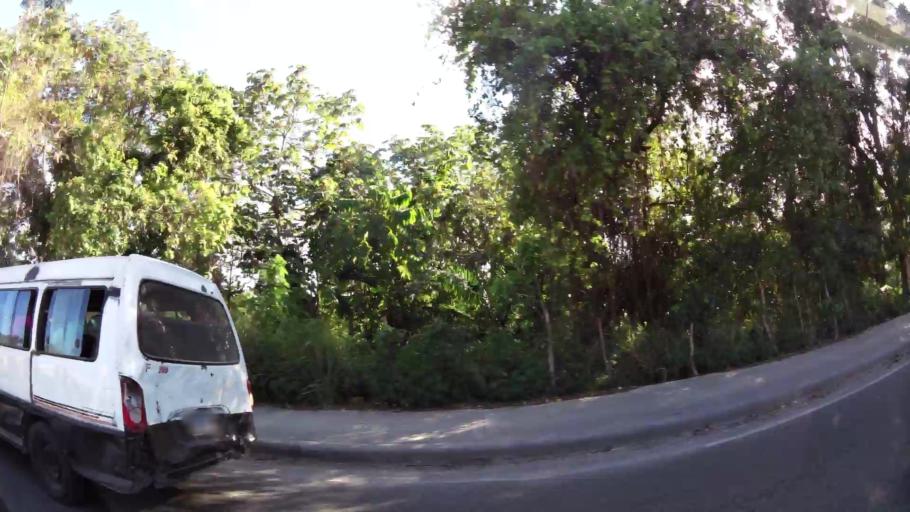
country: DO
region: Nacional
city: Santo Domingo
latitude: 18.5088
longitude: -69.9641
